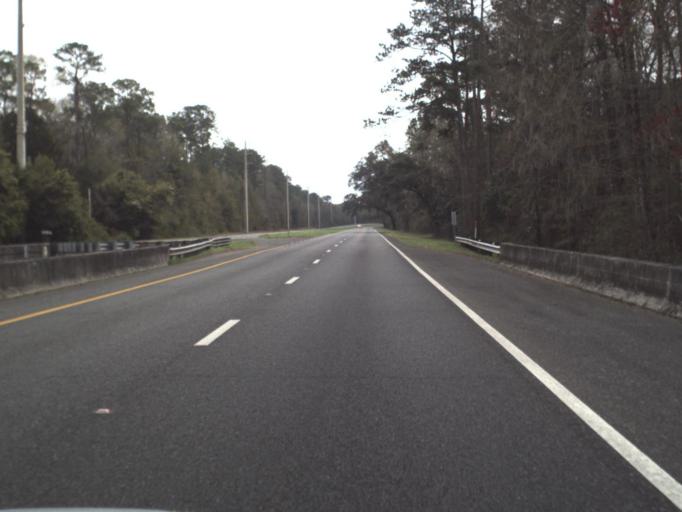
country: US
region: Florida
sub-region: Leon County
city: Tallahassee
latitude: 30.4206
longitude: -84.1011
